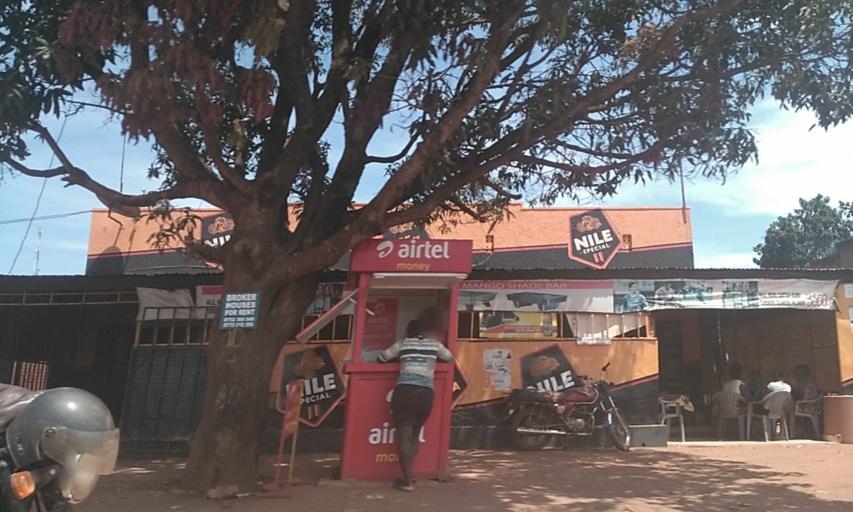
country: UG
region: Central Region
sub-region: Wakiso District
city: Wakiso
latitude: 0.4024
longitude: 32.4764
